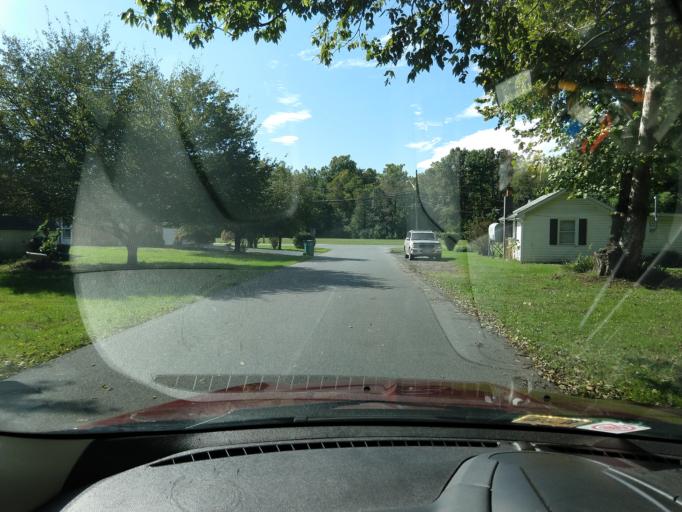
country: US
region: Virginia
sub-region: Rockingham County
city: Grottoes
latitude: 38.2649
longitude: -78.8312
